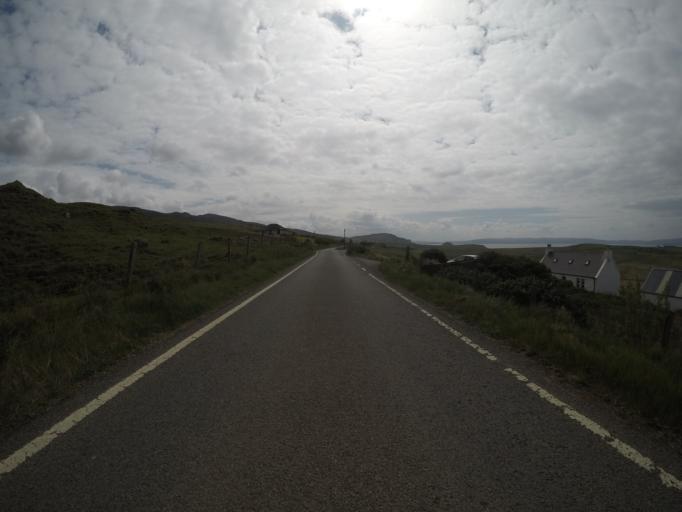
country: GB
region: Scotland
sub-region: Highland
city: Portree
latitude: 57.6254
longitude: -6.3774
